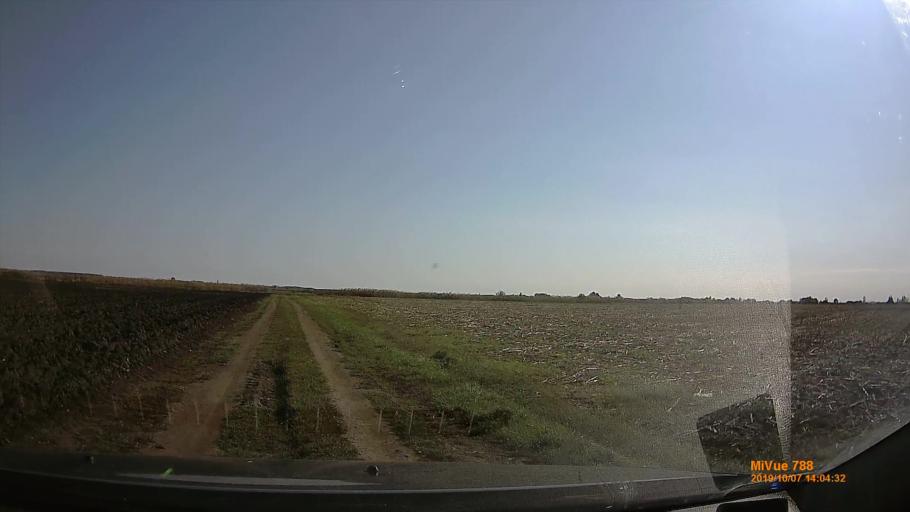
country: HU
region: Jasz-Nagykun-Szolnok
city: Cserkeszolo
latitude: 46.8763
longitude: 20.2265
